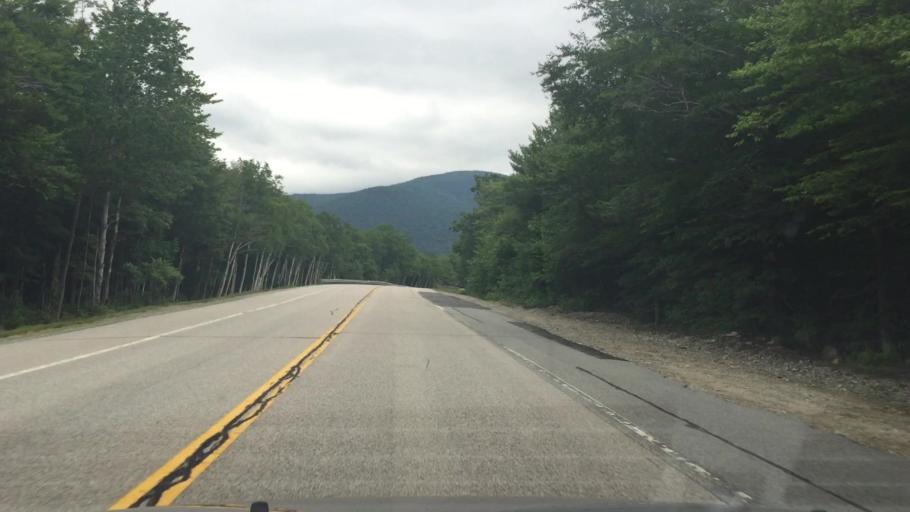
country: US
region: New Hampshire
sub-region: Grafton County
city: Deerfield
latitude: 44.1706
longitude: -71.3865
